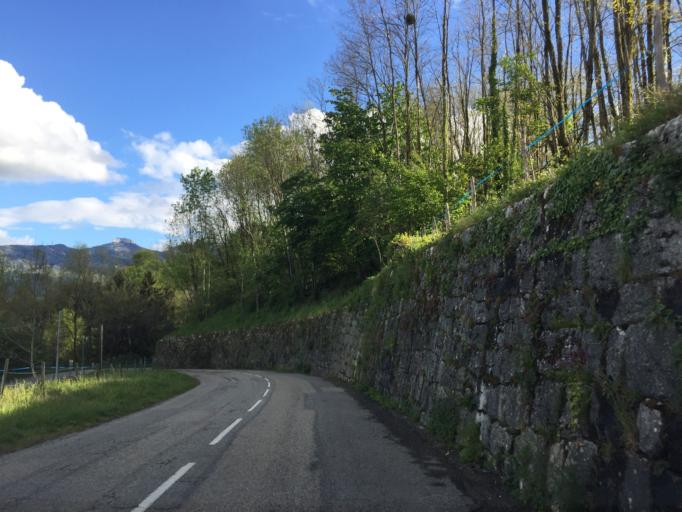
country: FR
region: Rhone-Alpes
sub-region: Departement de la Savoie
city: Vimines
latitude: 45.5651
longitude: 5.8453
